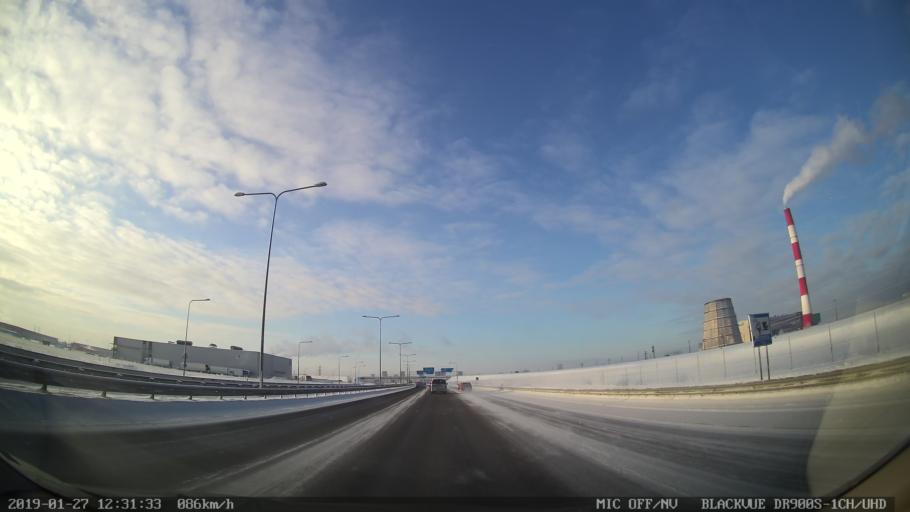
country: EE
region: Harju
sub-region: Joelaehtme vald
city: Loo
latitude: 59.4478
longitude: 24.9347
